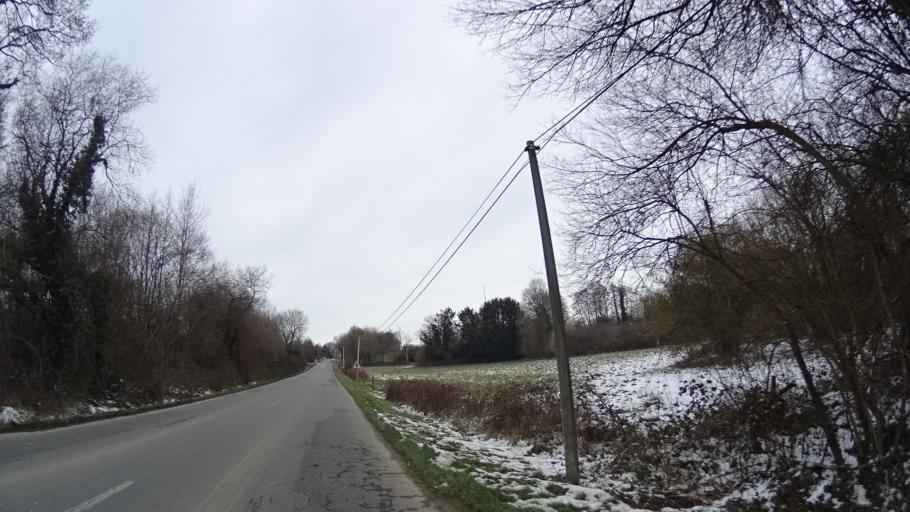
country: FR
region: Brittany
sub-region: Departement d'Ille-et-Vilaine
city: Irodouer
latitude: 48.2767
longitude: -1.9757
